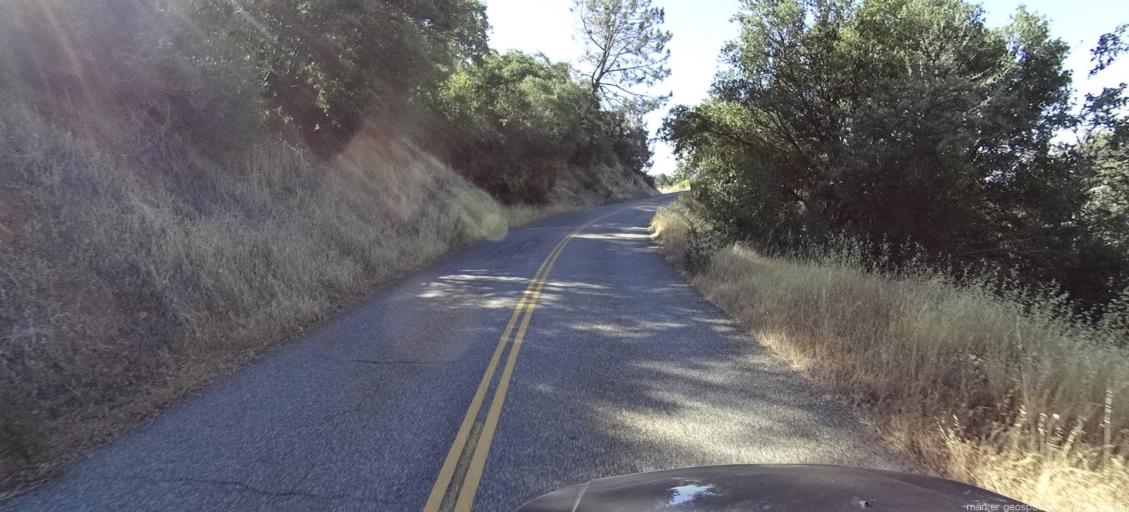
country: US
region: California
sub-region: Fresno County
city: Auberry
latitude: 37.1850
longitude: -119.4551
